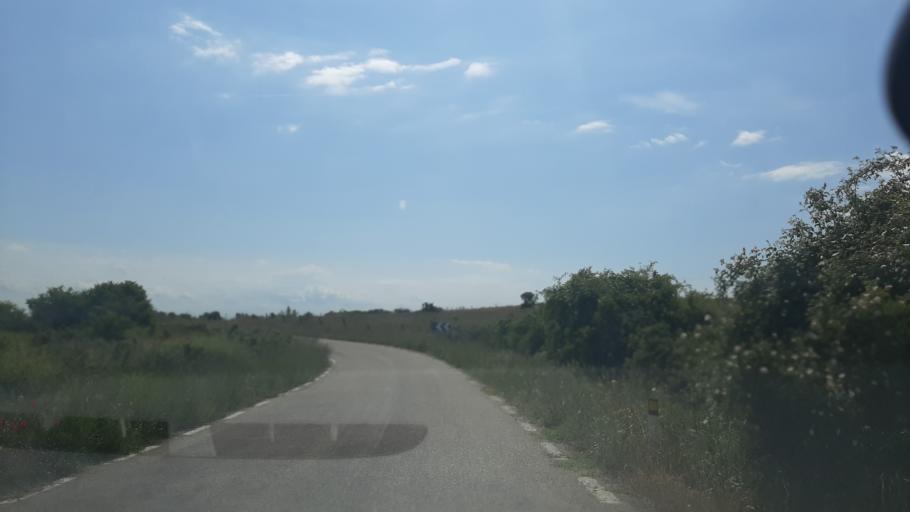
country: ES
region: Castille and Leon
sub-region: Provincia de Salamanca
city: Gallegos de Arganan
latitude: 40.6370
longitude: -6.7221
